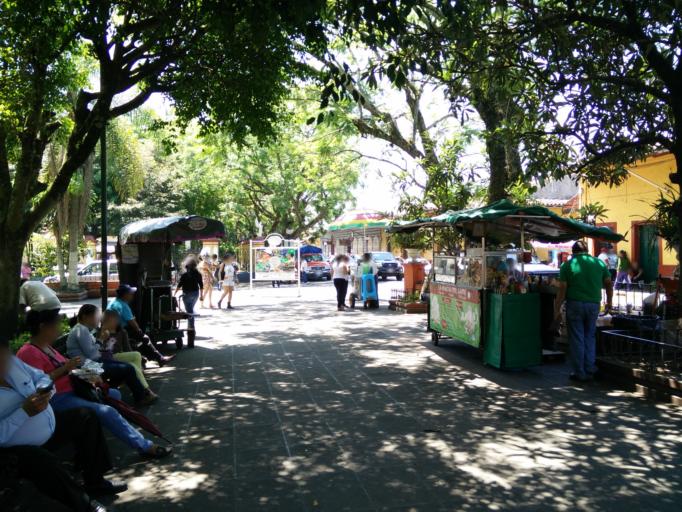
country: MX
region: Veracruz
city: Coatepec
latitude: 19.4541
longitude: -96.9596
